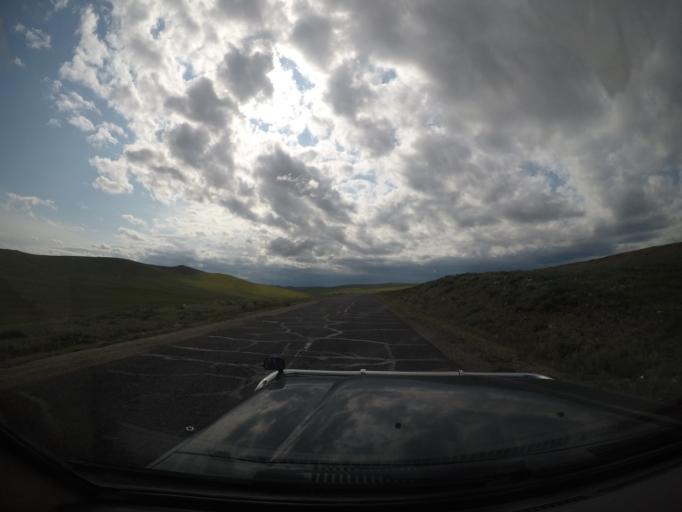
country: MN
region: Hentiy
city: Modot
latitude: 47.8054
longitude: 108.7219
